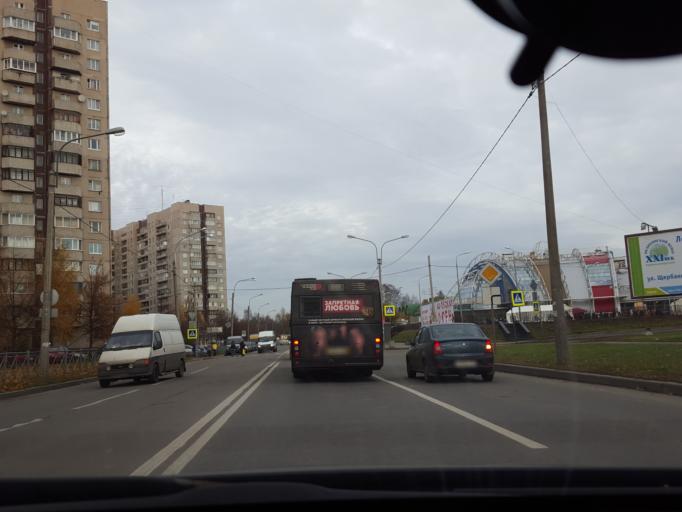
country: RU
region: St.-Petersburg
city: Kolomyagi
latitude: 60.0251
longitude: 30.3015
